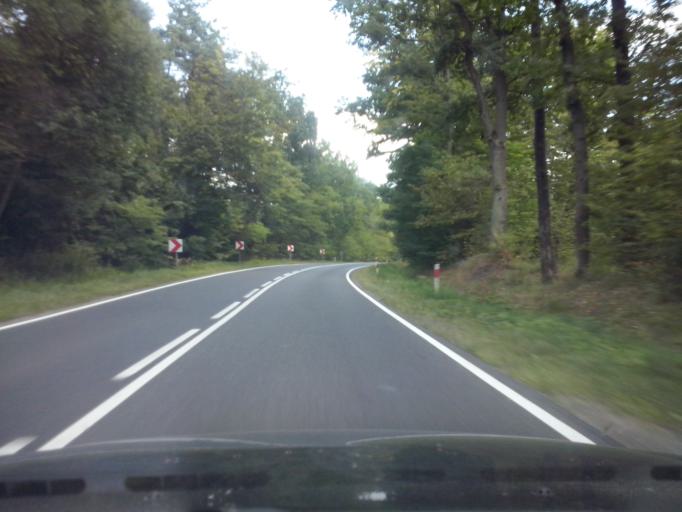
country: PL
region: Swietokrzyskie
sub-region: Powiat staszowski
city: Osiek
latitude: 50.5323
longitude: 21.4852
